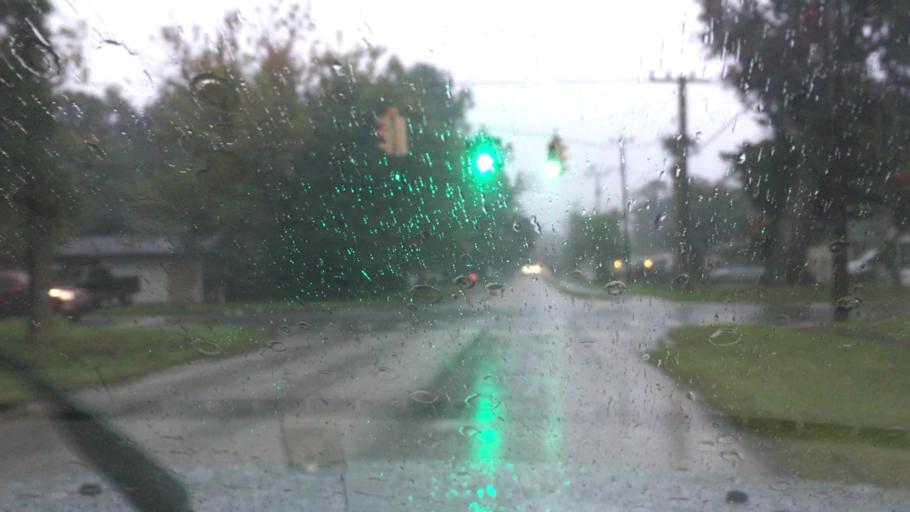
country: US
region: Florida
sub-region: Volusia County
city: Holly Hill
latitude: 29.2257
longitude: -81.0412
